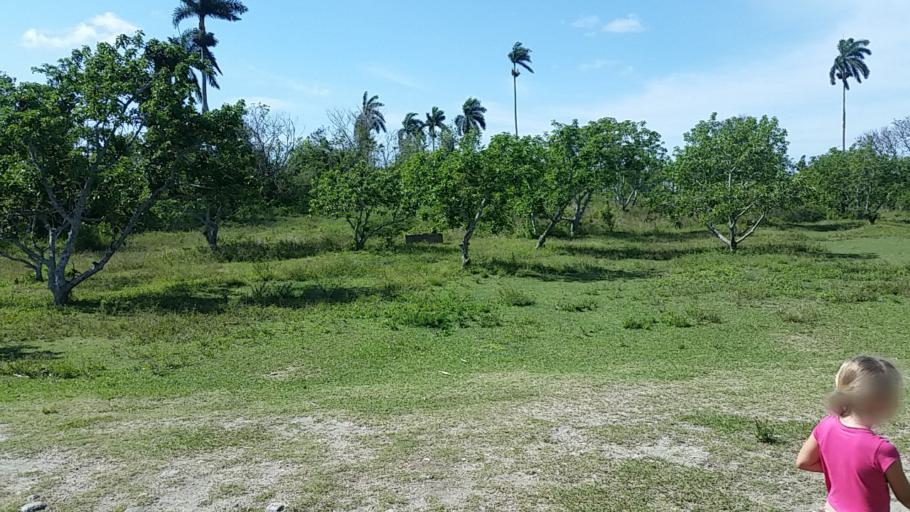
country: CU
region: Matanzas
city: Union de Reyes
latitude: 22.8405
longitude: -81.5590
